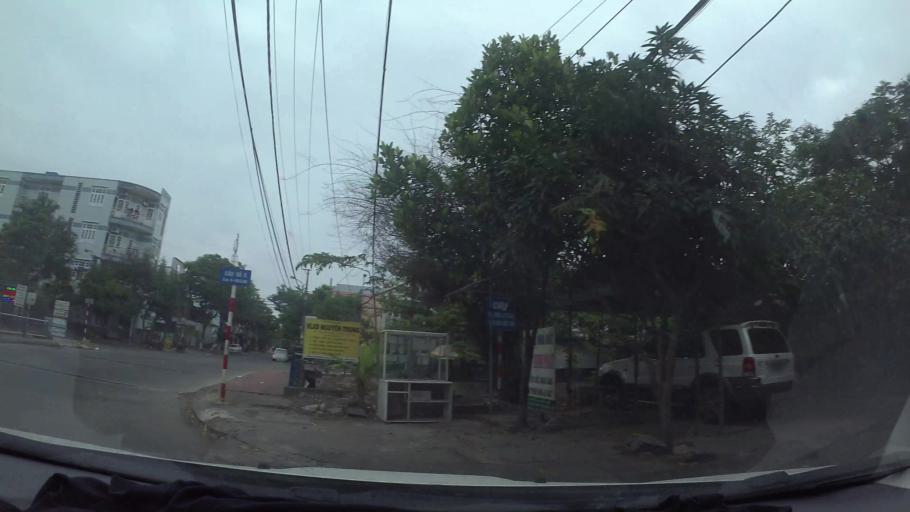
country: VN
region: Da Nang
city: Lien Chieu
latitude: 16.0785
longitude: 108.1610
